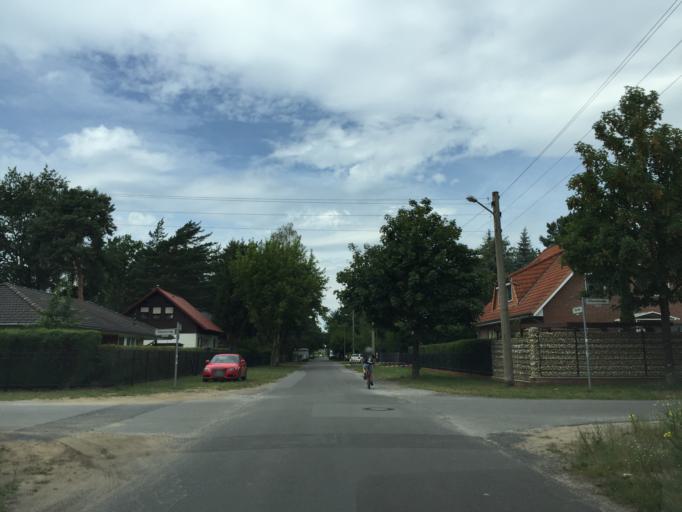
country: DE
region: Berlin
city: Mahlsdorf
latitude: 52.4893
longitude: 13.6181
